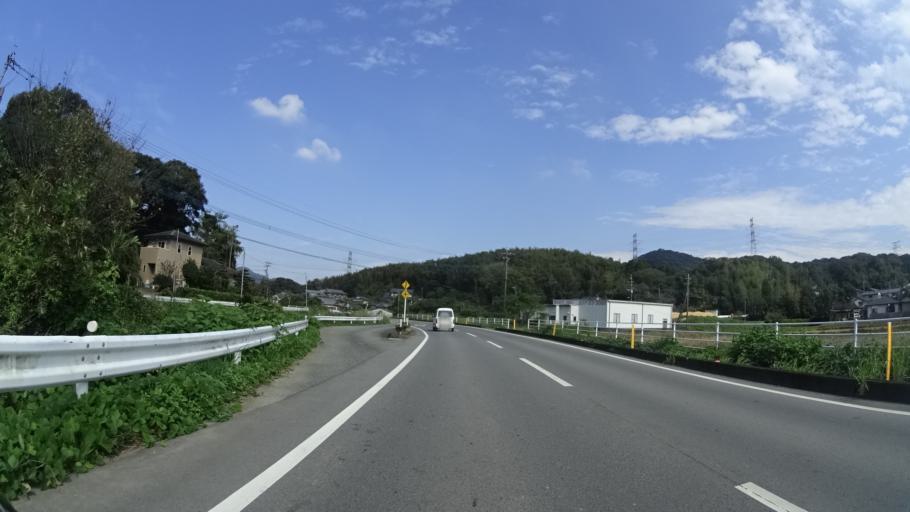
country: JP
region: Kumamoto
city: Matsubase
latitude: 32.6562
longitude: 130.7163
